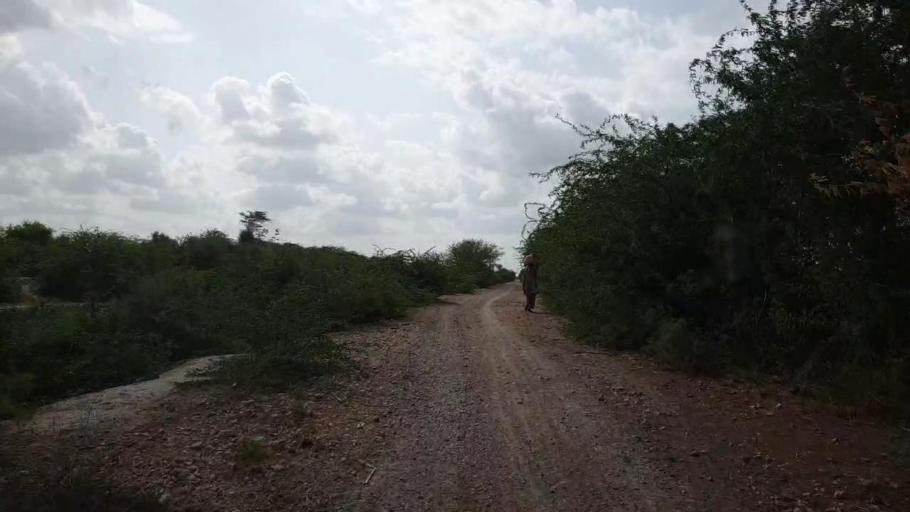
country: PK
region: Sindh
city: Kario
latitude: 24.6981
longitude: 68.6475
